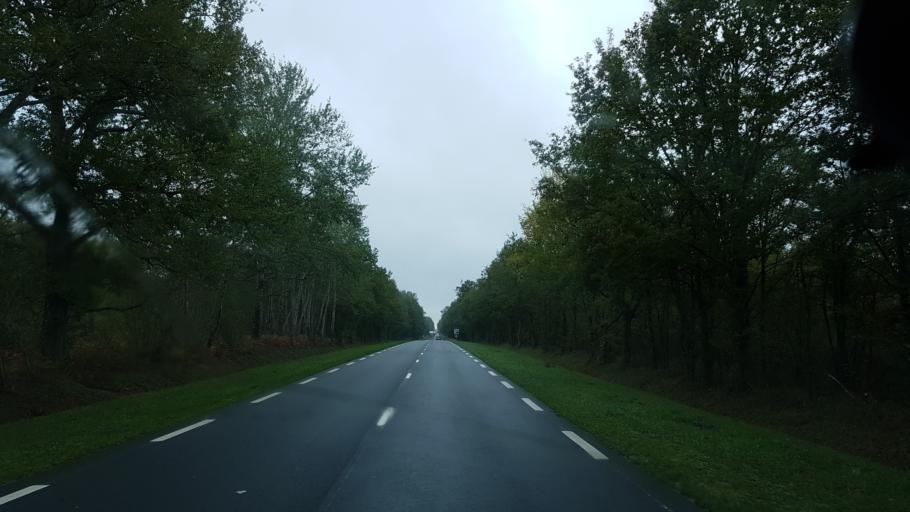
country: FR
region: Centre
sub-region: Departement du Loir-et-Cher
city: Salbris
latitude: 47.3980
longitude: 2.0546
